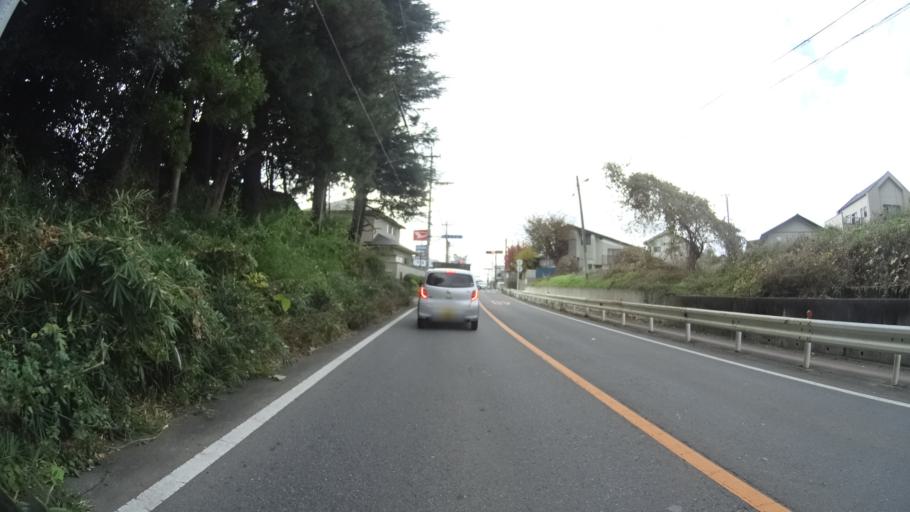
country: JP
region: Gunma
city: Maebashi-shi
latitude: 36.4043
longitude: 139.1249
